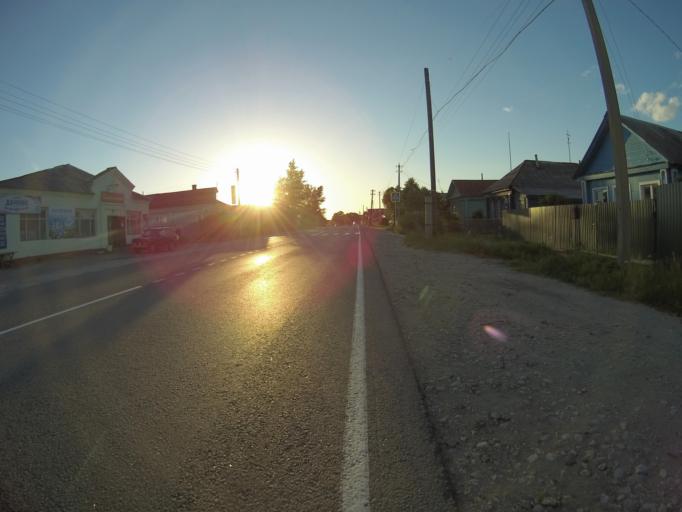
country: RU
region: Vladimir
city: Kommunar
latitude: 56.0420
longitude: 40.5455
